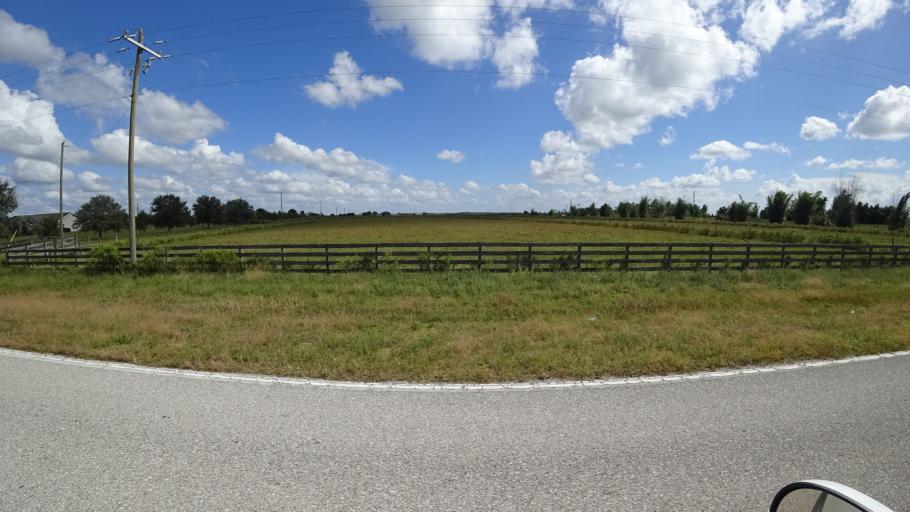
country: US
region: Florida
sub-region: Sarasota County
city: Warm Mineral Springs
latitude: 27.2965
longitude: -82.1896
